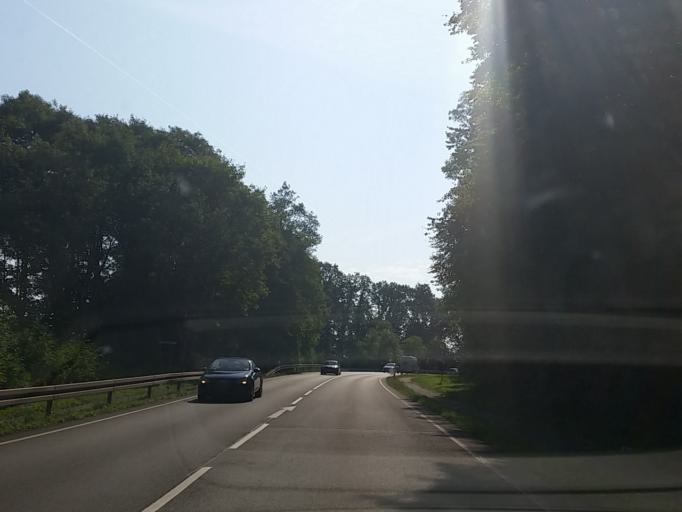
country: DE
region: Saarland
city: Schmelz
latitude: 49.4513
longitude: 6.8512
